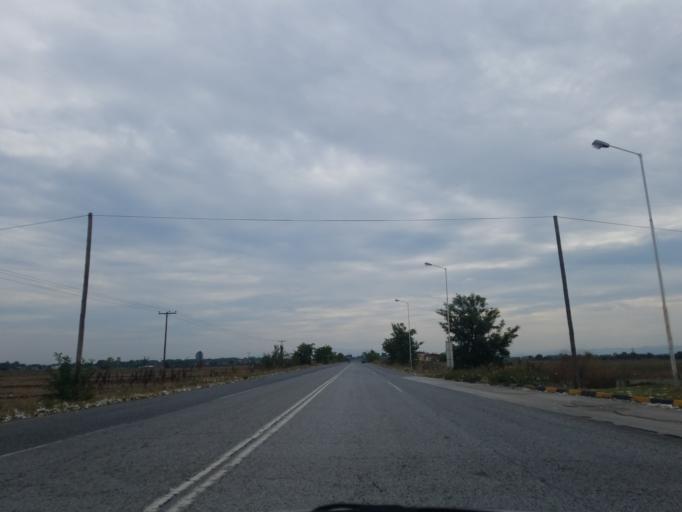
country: GR
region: Thessaly
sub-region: Nomos Kardhitsas
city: Sofades
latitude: 39.3485
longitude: 22.0696
